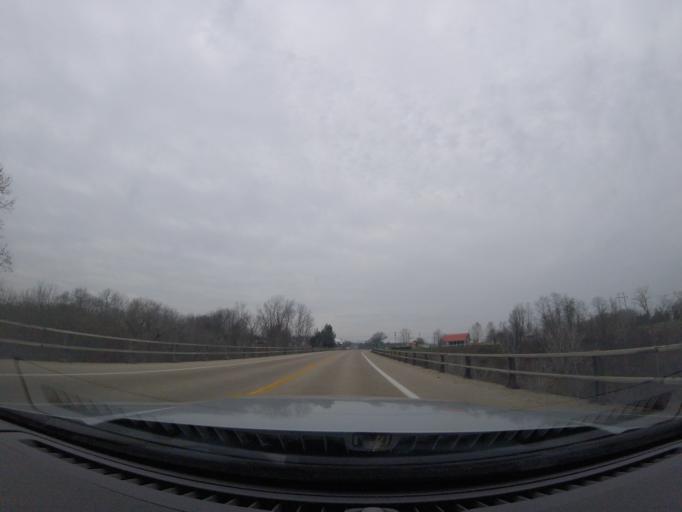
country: US
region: New York
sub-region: Yates County
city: Penn Yan
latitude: 42.6794
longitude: -76.9611
